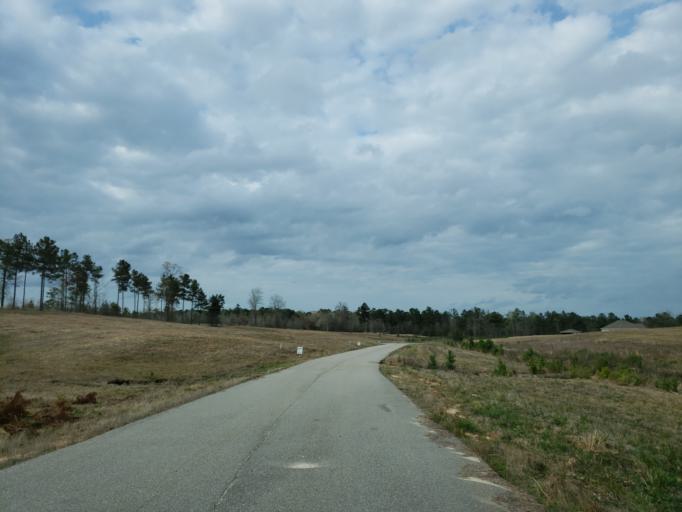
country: US
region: Mississippi
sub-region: Jones County
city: Ellisville
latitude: 31.5621
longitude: -89.2537
